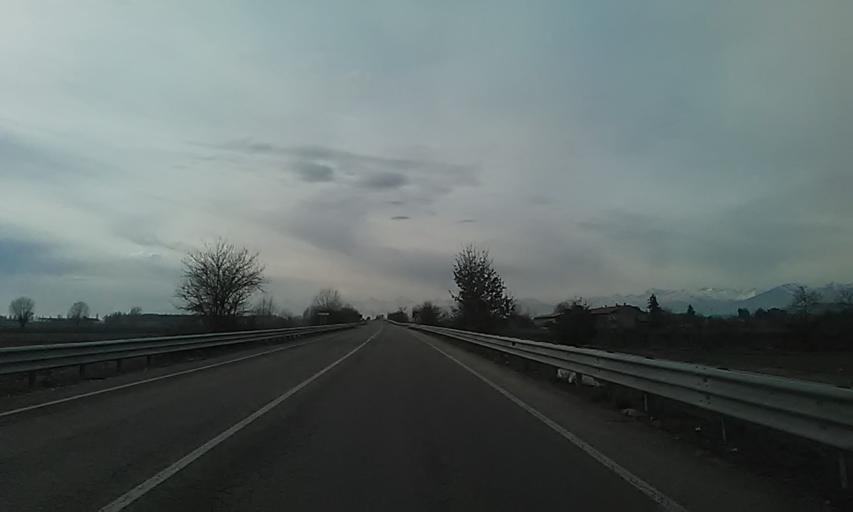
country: IT
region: Piedmont
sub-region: Provincia di Vercelli
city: Cigliano
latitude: 45.2976
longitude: 8.0177
